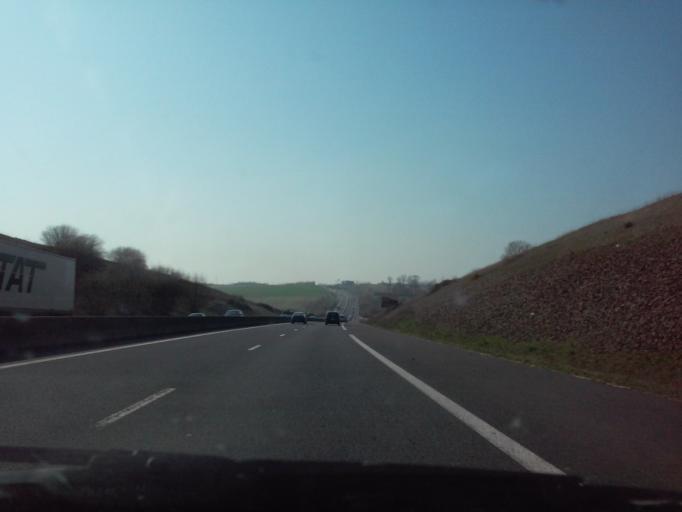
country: FR
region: Lower Normandy
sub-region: Departement du Calvados
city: Saint-Vigor-le-Grand
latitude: 49.2487
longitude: -0.6283
